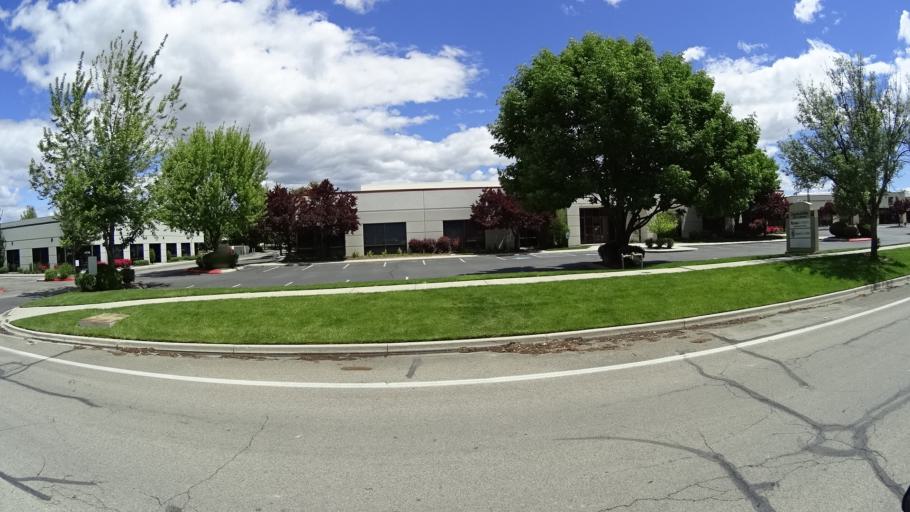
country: US
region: Idaho
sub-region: Ada County
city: Eagle
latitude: 43.6601
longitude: -116.3411
